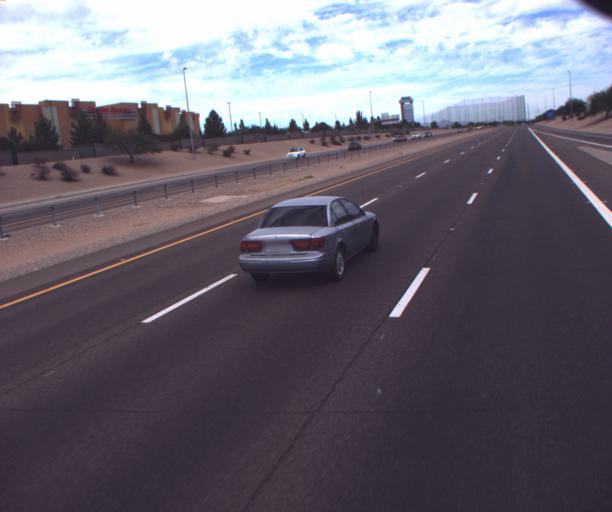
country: US
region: Arizona
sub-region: Maricopa County
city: Gilbert
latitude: 33.3100
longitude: -111.7392
